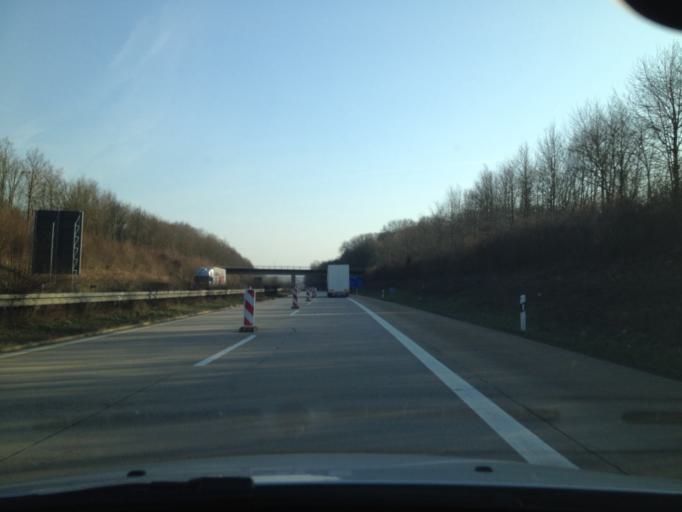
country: DE
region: Bavaria
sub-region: Regierungsbezirk Mittelfranken
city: Gollhofen
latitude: 49.5816
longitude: 10.1715
